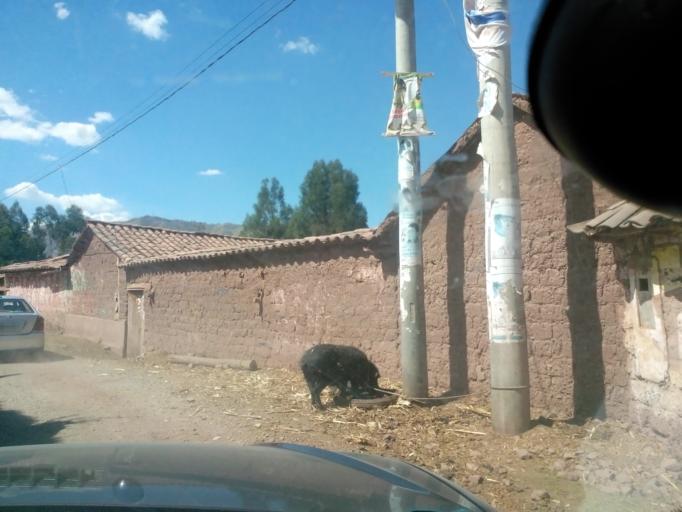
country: PE
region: Cusco
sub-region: Provincia de Anta
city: Zurite
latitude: -13.4372
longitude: -72.2291
